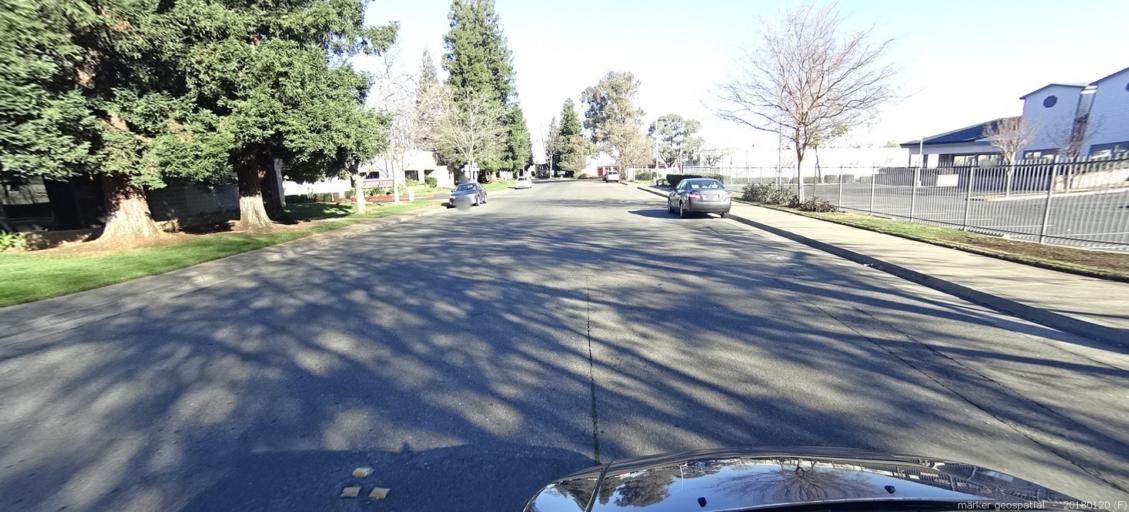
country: US
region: California
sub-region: Sacramento County
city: Rancho Cordova
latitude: 38.5745
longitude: -121.3068
